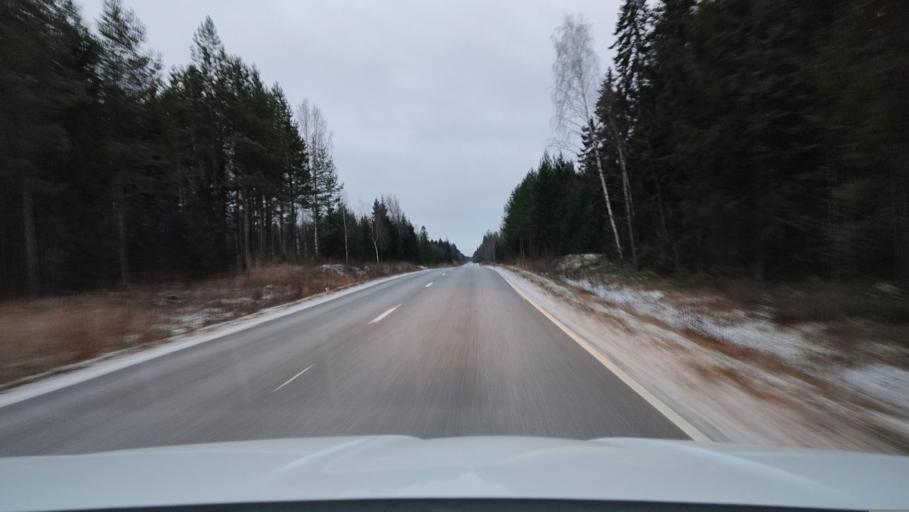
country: FI
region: Ostrobothnia
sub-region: Vaasa
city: Replot
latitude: 63.2601
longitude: 21.3631
